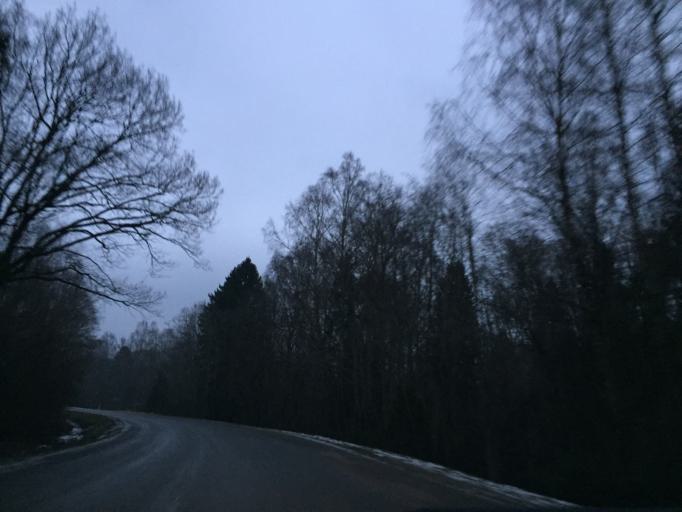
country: EE
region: Saare
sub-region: Kuressaare linn
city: Kuressaare
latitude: 58.5716
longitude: 22.6697
